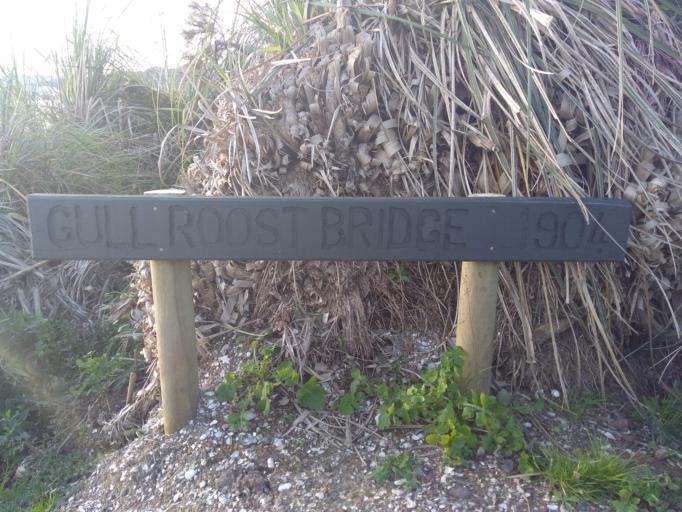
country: NZ
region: Northland
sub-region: Whangarei
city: Whangarei
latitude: -35.7478
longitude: 174.3514
